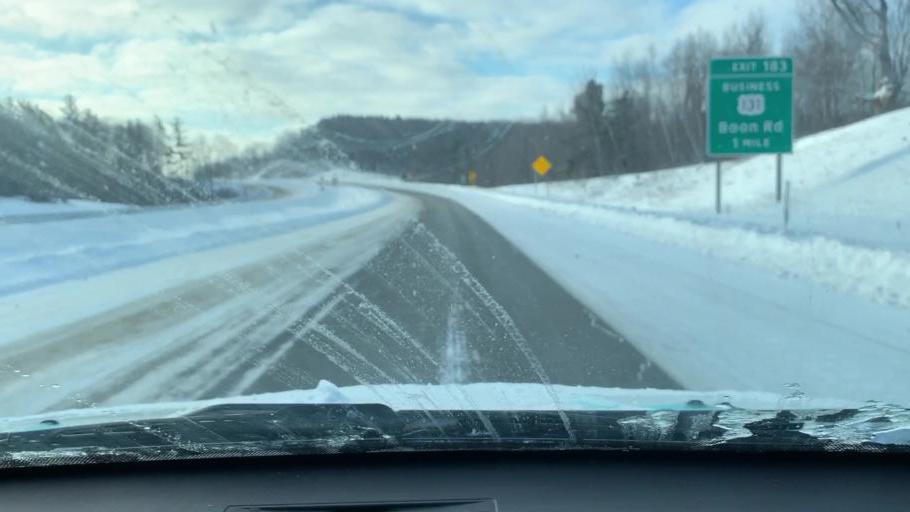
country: US
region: Michigan
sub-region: Wexford County
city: Cadillac
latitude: 44.3017
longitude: -85.3925
